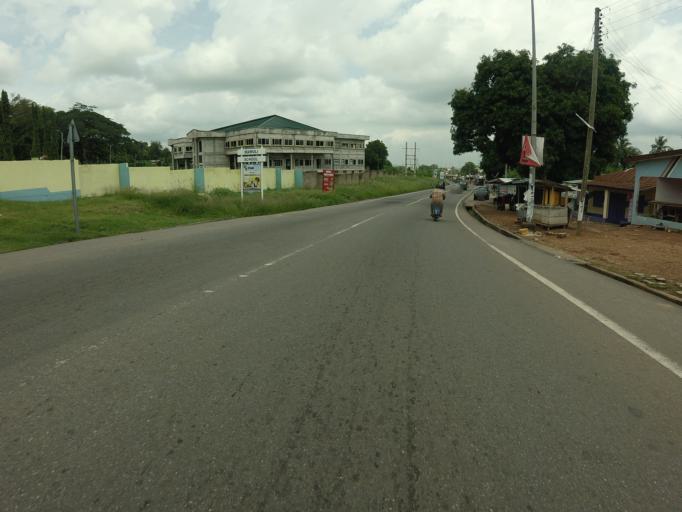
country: GH
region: Volta
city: Ho
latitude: 6.5986
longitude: 0.4727
